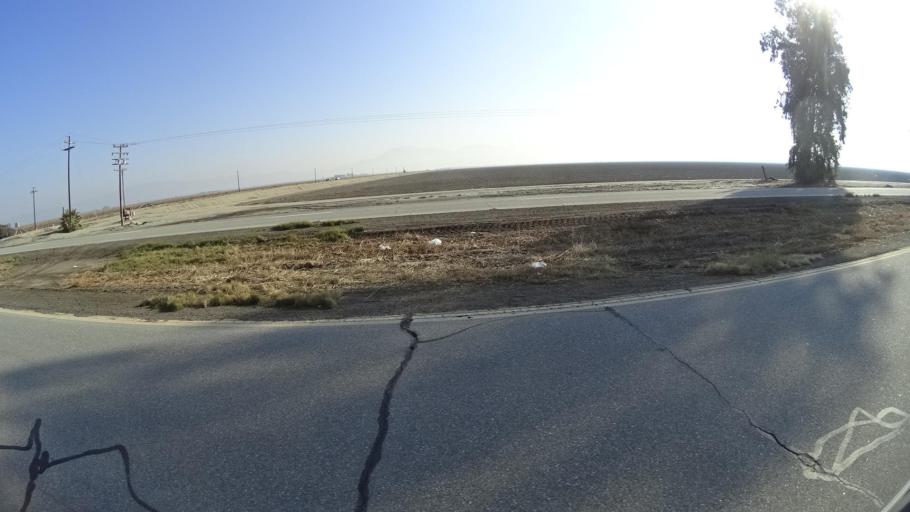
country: US
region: California
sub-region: Kern County
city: Greenfield
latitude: 35.1788
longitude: -119.0035
